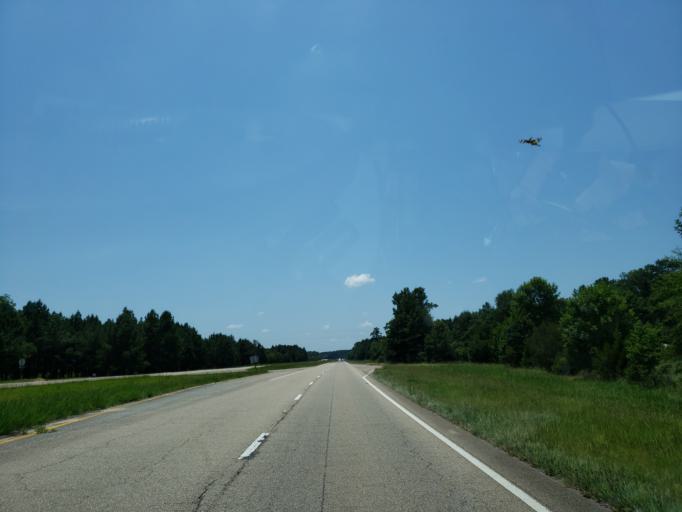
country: US
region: Mississippi
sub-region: Clarke County
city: Quitman
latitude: 31.8778
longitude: -88.7132
